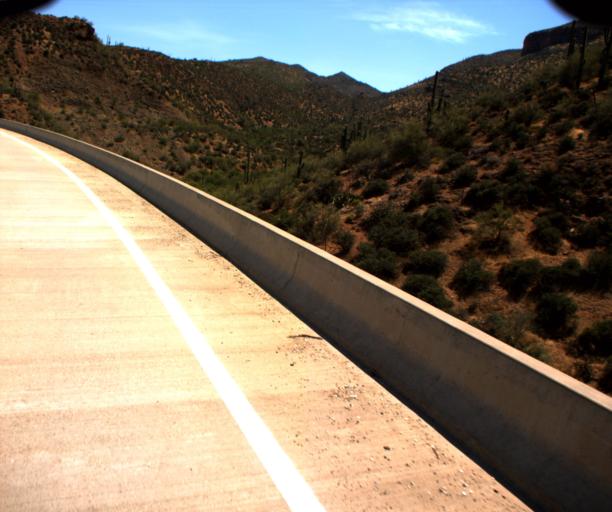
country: US
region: Arizona
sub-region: Gila County
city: Tonto Basin
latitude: 33.6708
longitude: -111.1438
